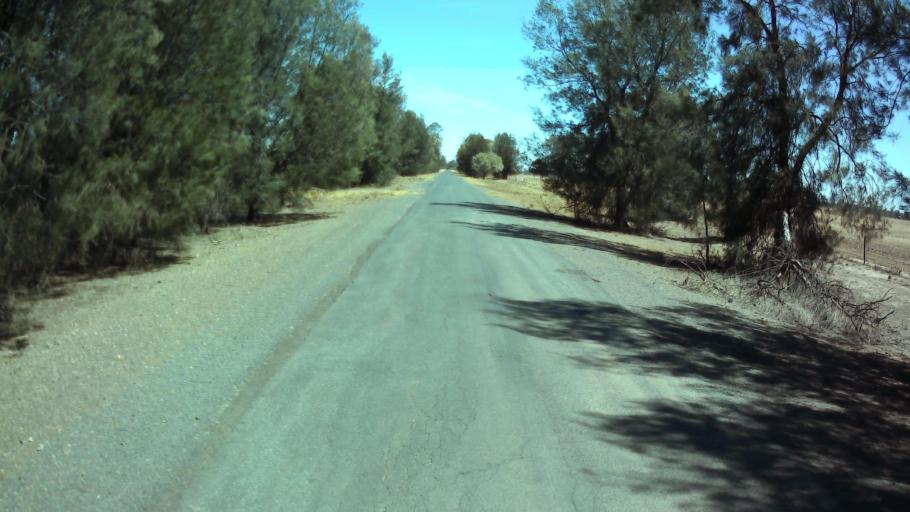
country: AU
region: New South Wales
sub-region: Weddin
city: Grenfell
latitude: -33.8862
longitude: 147.6891
